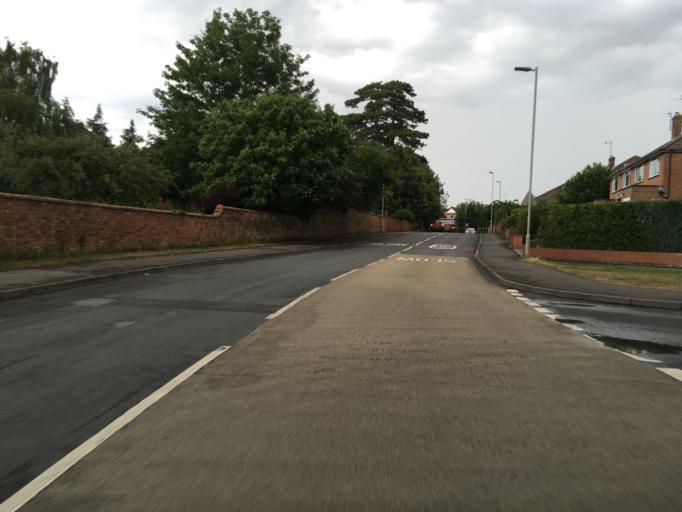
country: GB
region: England
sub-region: Gloucestershire
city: Barnwood
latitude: 51.8580
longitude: -2.1988
